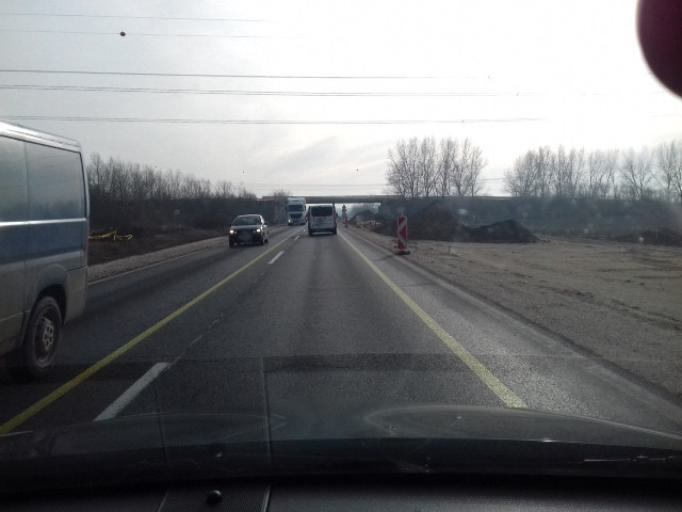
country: HU
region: Pest
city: Szod
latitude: 47.6972
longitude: 19.1703
